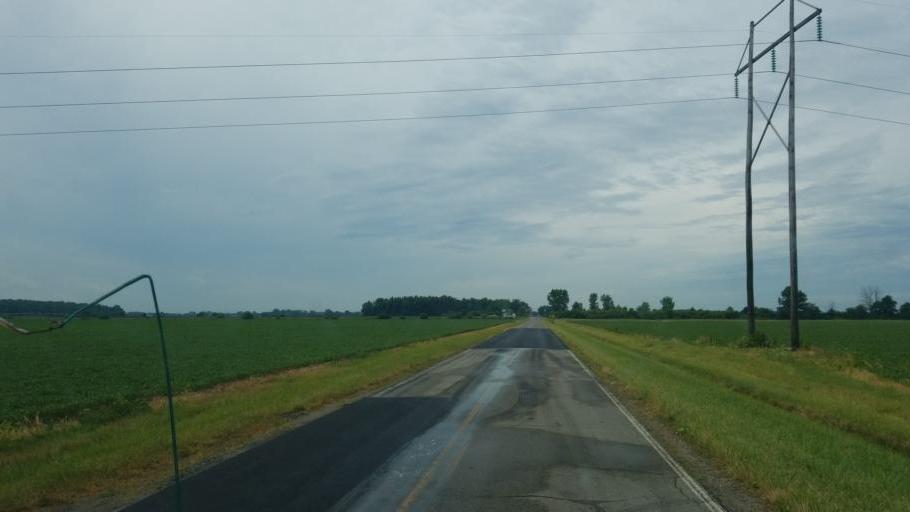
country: US
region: Ohio
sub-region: Defiance County
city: Hicksville
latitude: 41.2957
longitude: -84.6896
